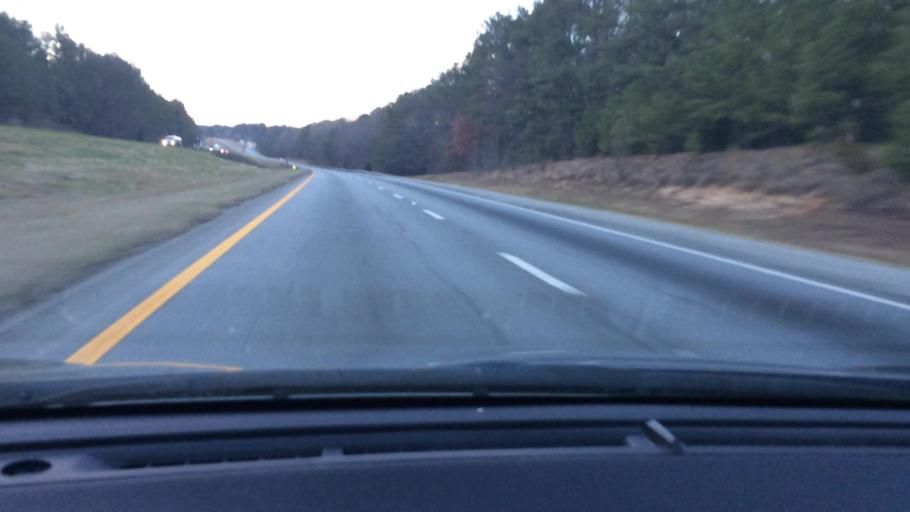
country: US
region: South Carolina
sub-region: Laurens County
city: Joanna
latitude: 34.4039
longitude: -81.6963
